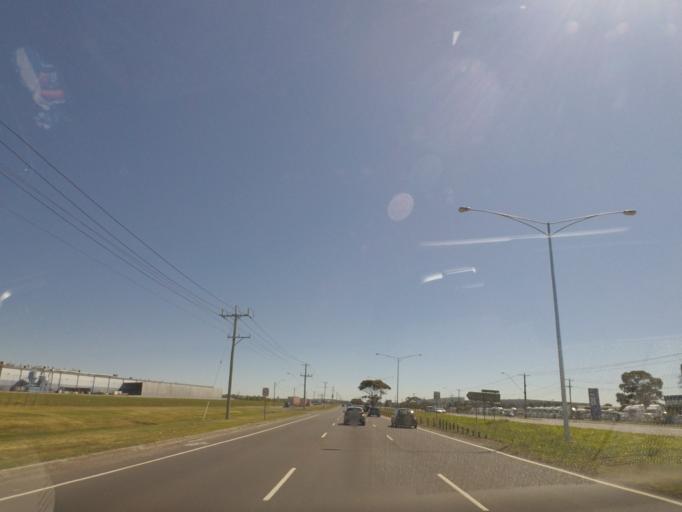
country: AU
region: Victoria
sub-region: Hume
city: Coolaroo
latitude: -37.6429
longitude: 144.9510
